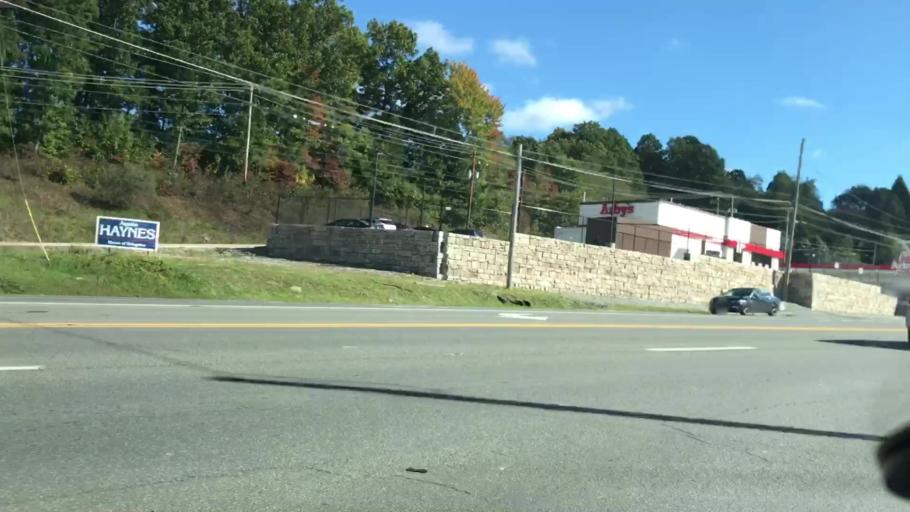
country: US
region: West Virginia
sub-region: Raleigh County
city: Prosperity
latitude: 37.8478
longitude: -81.1958
